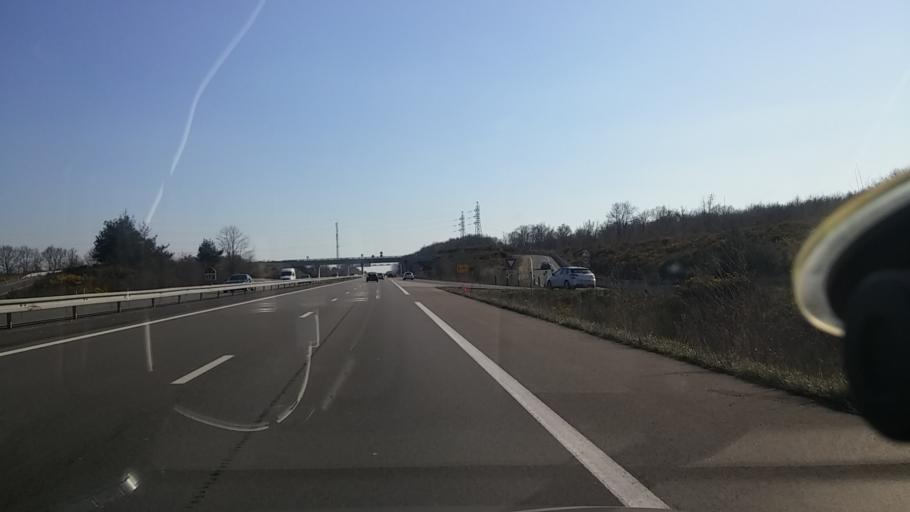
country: FR
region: Centre
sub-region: Departement du Loir-et-Cher
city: Theillay
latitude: 47.2887
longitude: 2.0437
